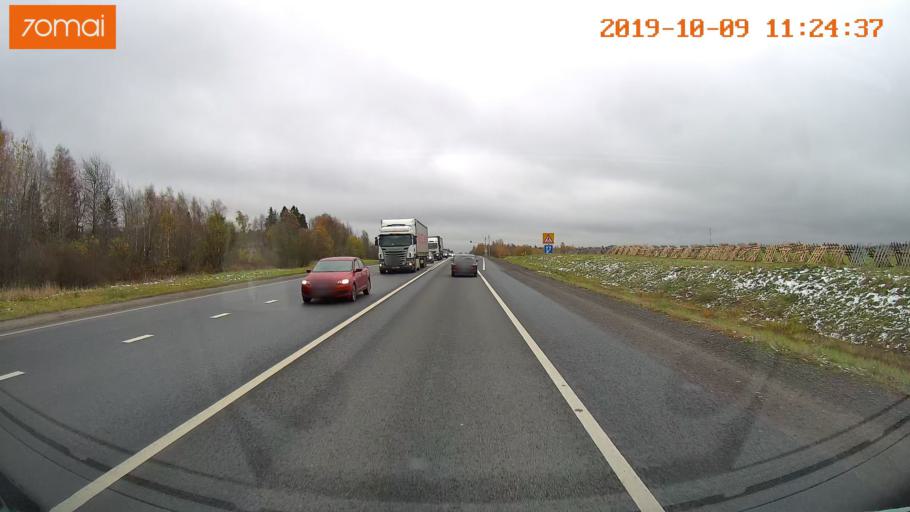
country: RU
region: Vologda
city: Vologda
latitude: 59.1099
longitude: 39.9817
